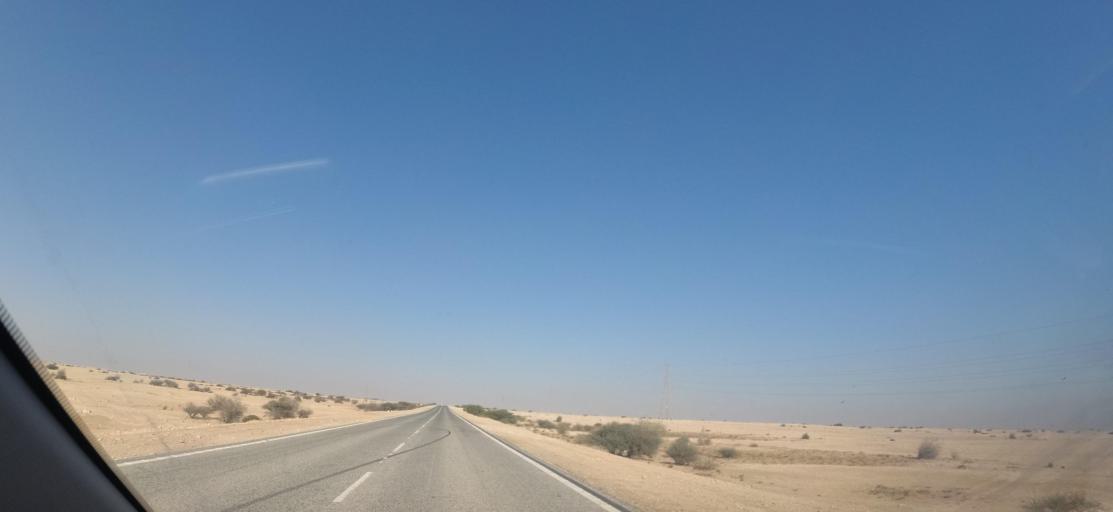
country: QA
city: Al Jumayliyah
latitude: 25.6333
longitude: 51.0976
